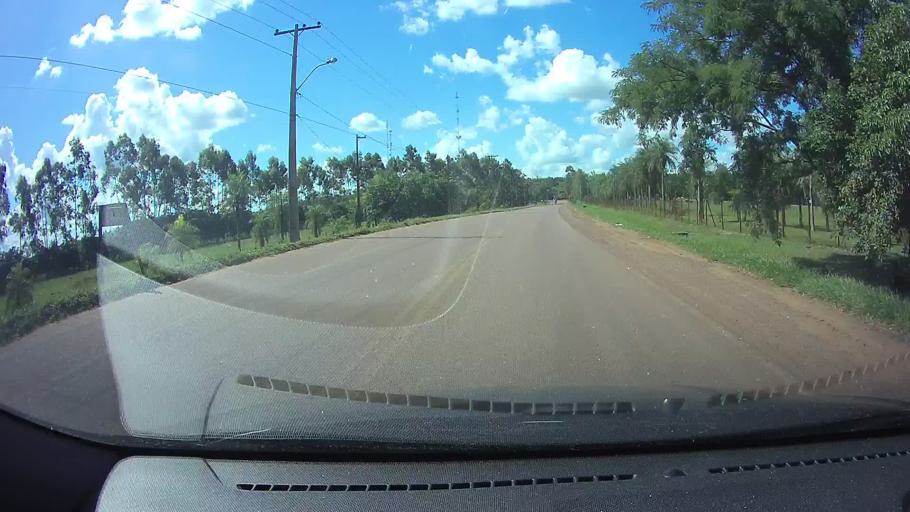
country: PY
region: Guaira
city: Coronel Martinez
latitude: -25.7750
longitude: -56.6519
